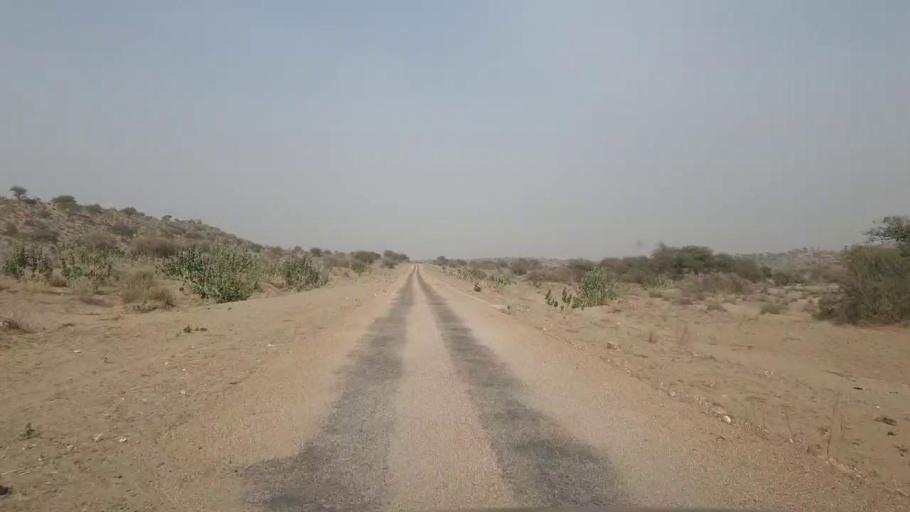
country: PK
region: Sindh
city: Chor
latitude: 25.6336
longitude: 69.9492
